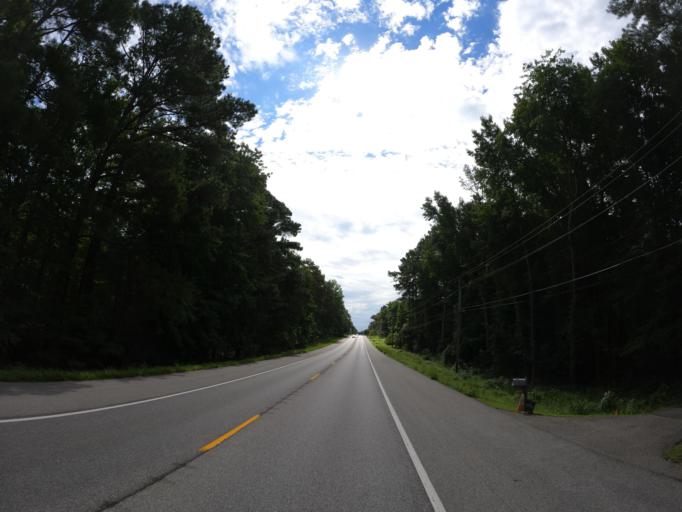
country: US
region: Maryland
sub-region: Saint Mary's County
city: California
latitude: 38.2427
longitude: -76.5643
